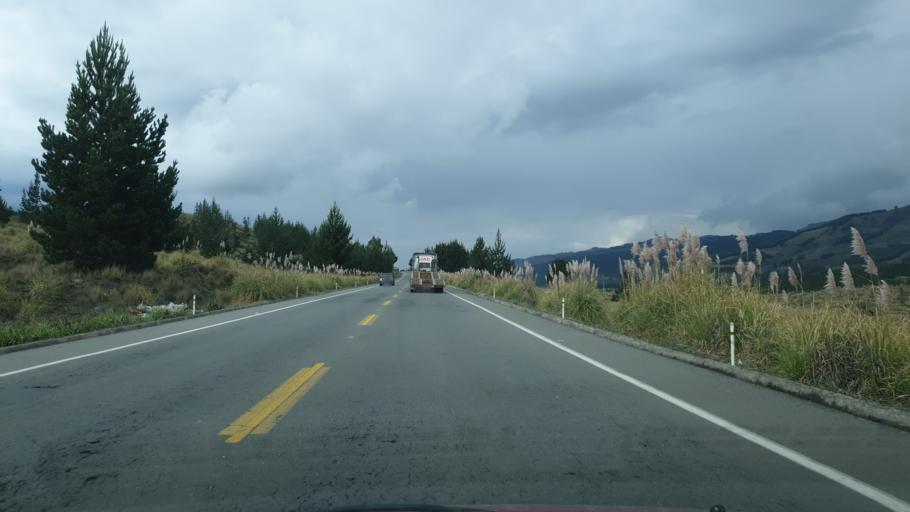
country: EC
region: Chimborazo
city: Alausi
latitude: -2.0438
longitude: -78.7390
